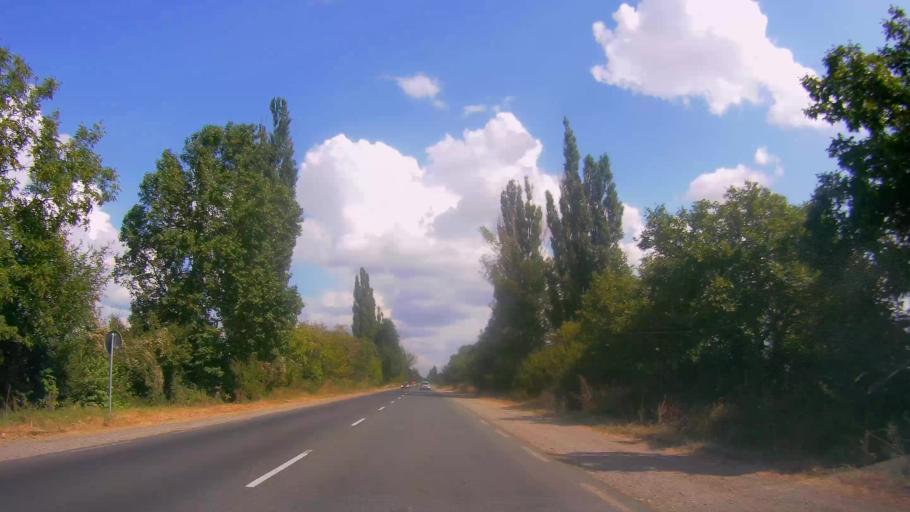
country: BG
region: Sliven
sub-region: Obshtina Sliven
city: Sliven
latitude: 42.6372
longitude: 26.2486
